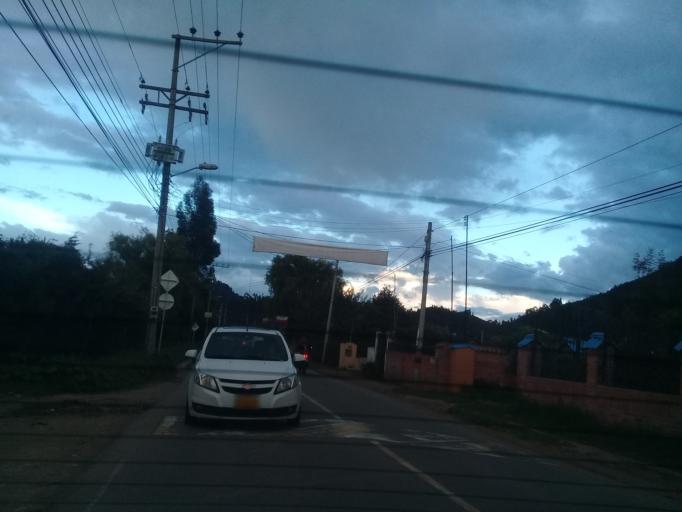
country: CO
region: Cundinamarca
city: Tabio
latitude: 4.9232
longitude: -74.0832
